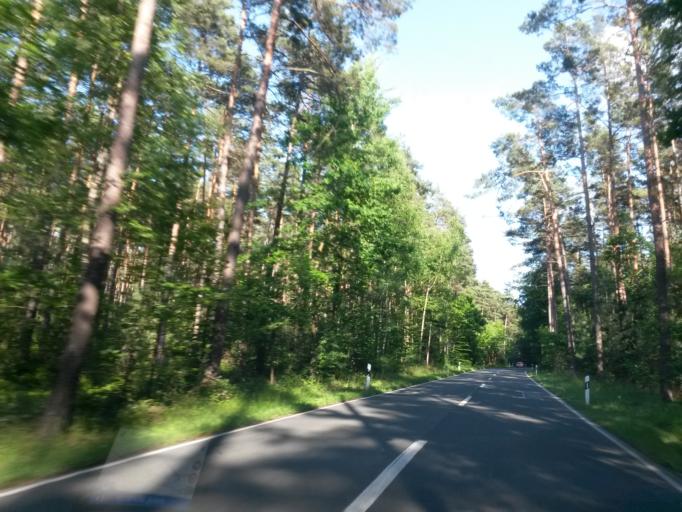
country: DE
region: Bavaria
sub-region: Regierungsbezirk Mittelfranken
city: Zirndorf
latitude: 49.4649
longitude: 10.9216
